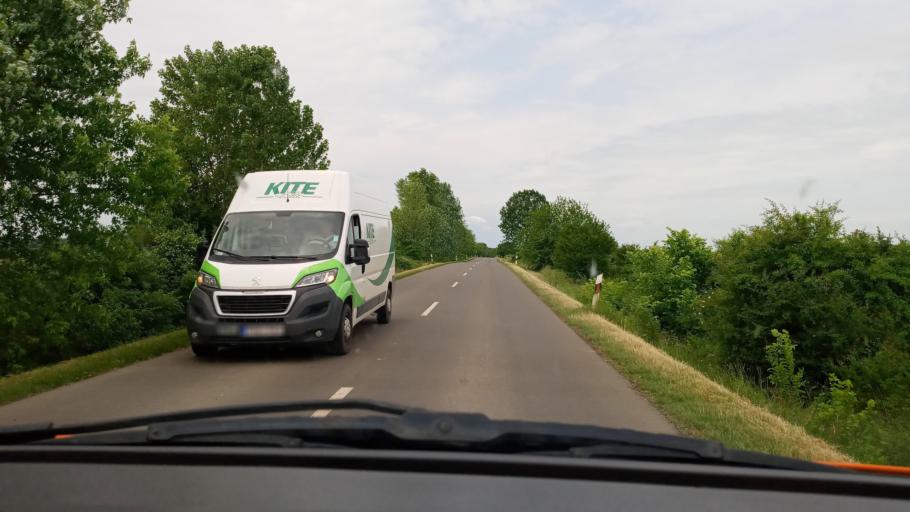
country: HU
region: Baranya
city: Vajszlo
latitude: 45.8925
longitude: 18.0261
